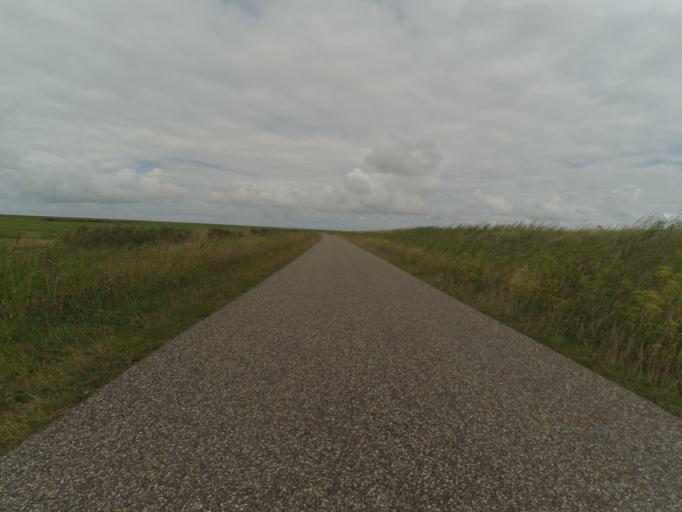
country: NL
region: Friesland
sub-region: Gemeente Dongeradeel
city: Anjum
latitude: 53.3959
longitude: 6.1513
